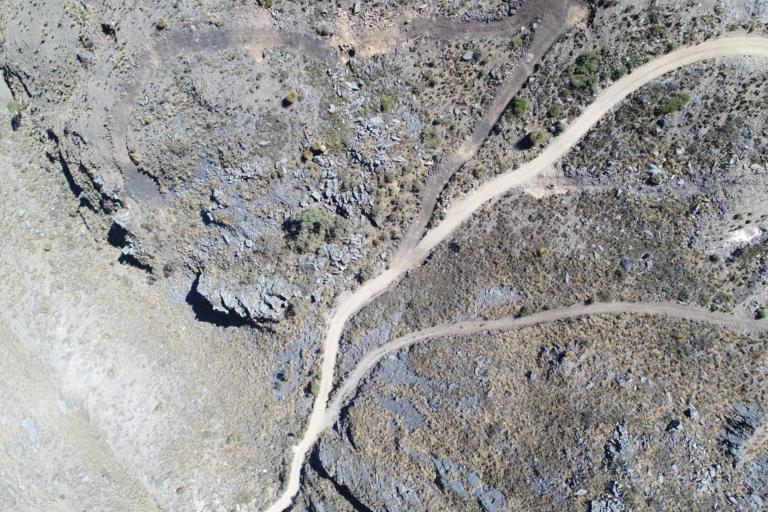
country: BO
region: La Paz
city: Viloco
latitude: -16.8054
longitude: -67.5543
